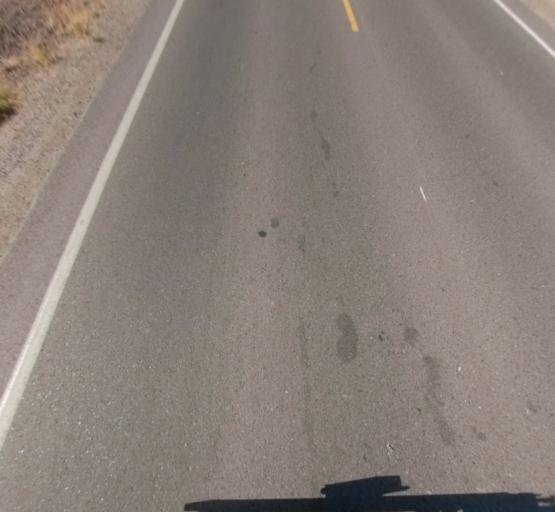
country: US
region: California
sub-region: Madera County
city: Madera
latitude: 36.9557
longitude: -120.1284
